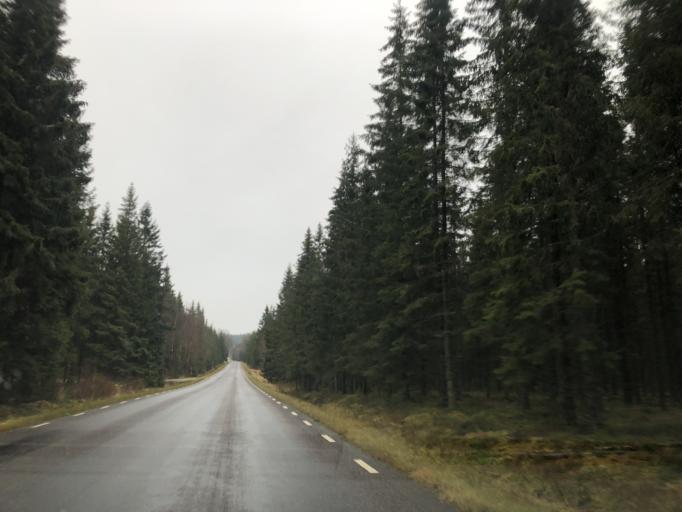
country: SE
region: Vaestra Goetaland
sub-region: Ulricehamns Kommun
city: Ulricehamn
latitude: 57.7321
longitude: 13.5444
